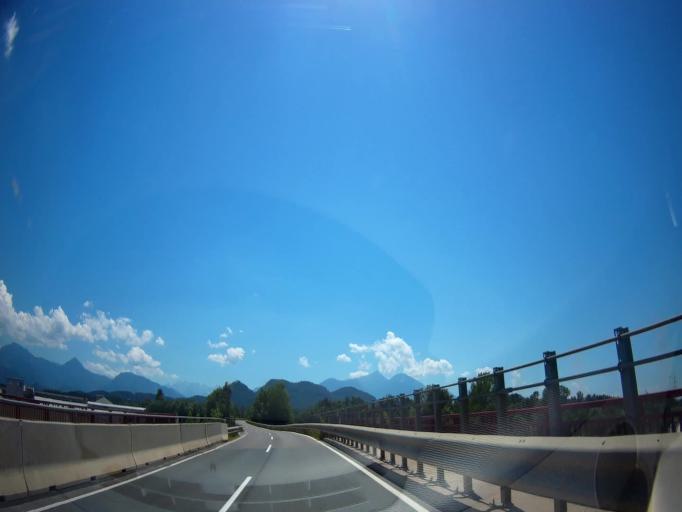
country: AT
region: Carinthia
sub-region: Politischer Bezirk Volkermarkt
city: Voelkermarkt
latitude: 46.6241
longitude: 14.6159
